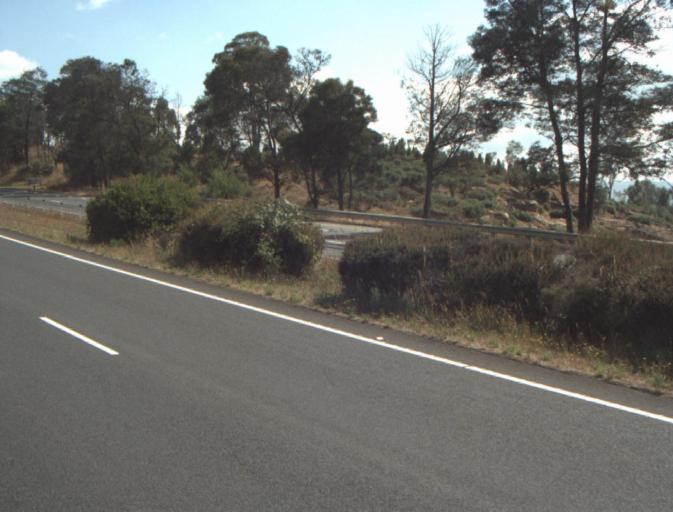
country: AU
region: Tasmania
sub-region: Launceston
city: Summerhill
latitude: -41.4833
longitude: 147.1501
